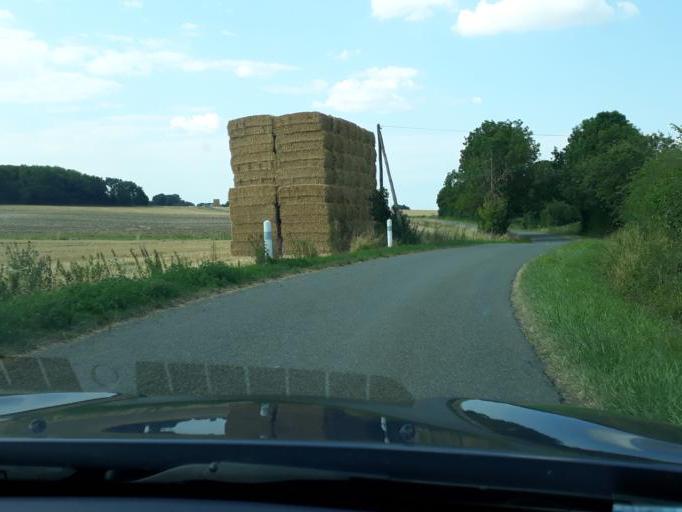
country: FR
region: Centre
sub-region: Departement du Cher
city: Nerondes
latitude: 47.0326
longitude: 2.8980
